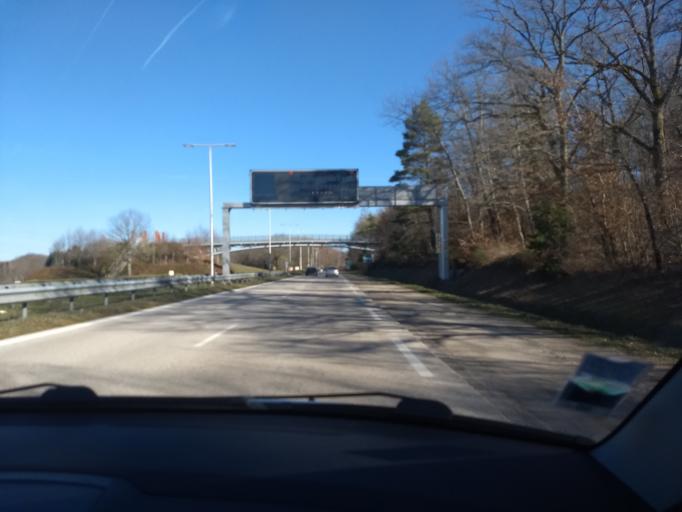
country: FR
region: Limousin
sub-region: Departement de la Haute-Vienne
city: Couzeix
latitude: 45.8658
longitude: 1.2763
